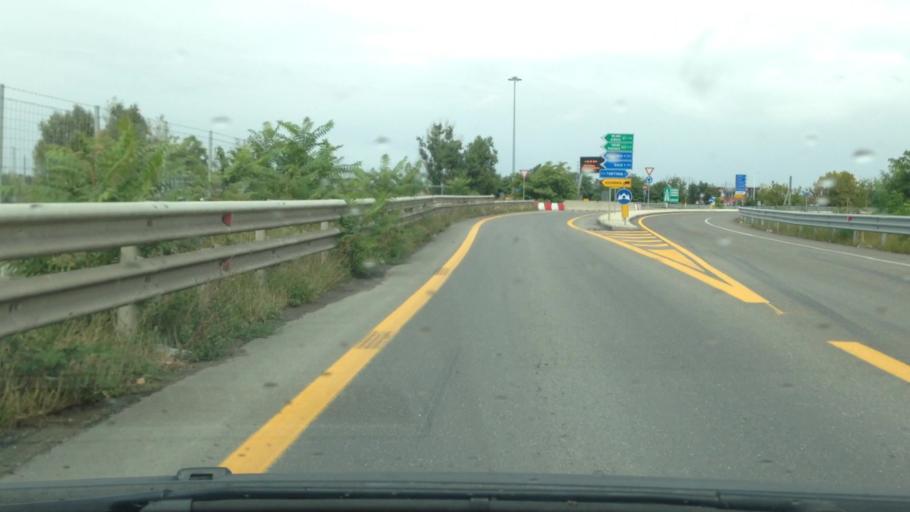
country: IT
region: Piedmont
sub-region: Provincia di Alessandria
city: Tortona
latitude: 44.9065
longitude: 8.8375
